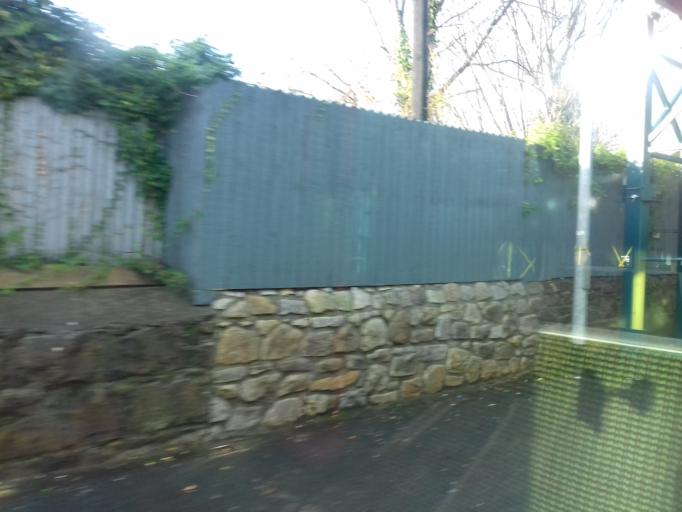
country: IE
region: Leinster
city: Donnybrook
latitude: 53.3205
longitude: -6.2112
